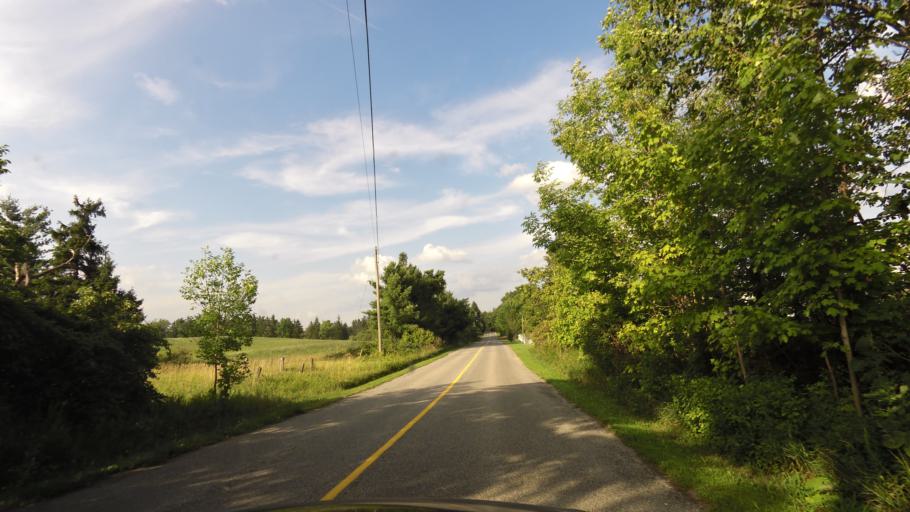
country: CA
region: Ontario
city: Burlington
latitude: 43.3856
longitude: -79.8646
